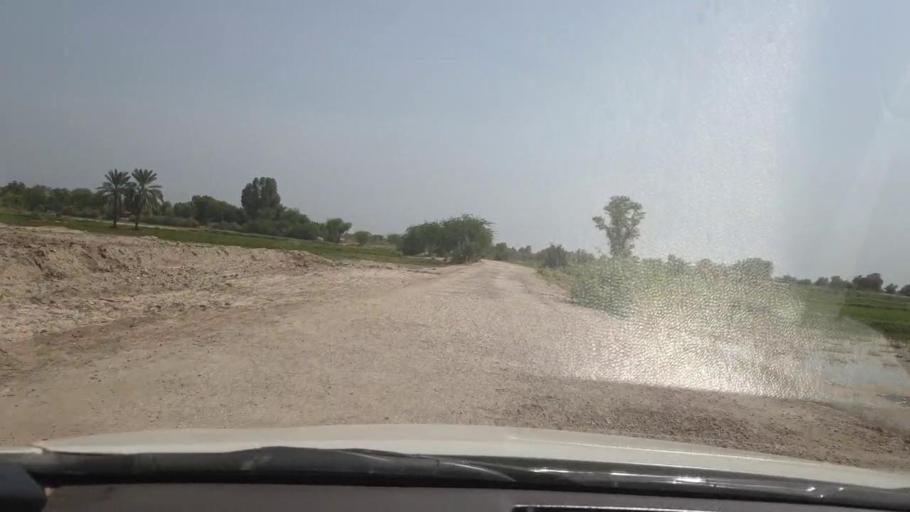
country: PK
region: Sindh
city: Shikarpur
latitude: 27.9314
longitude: 68.6037
